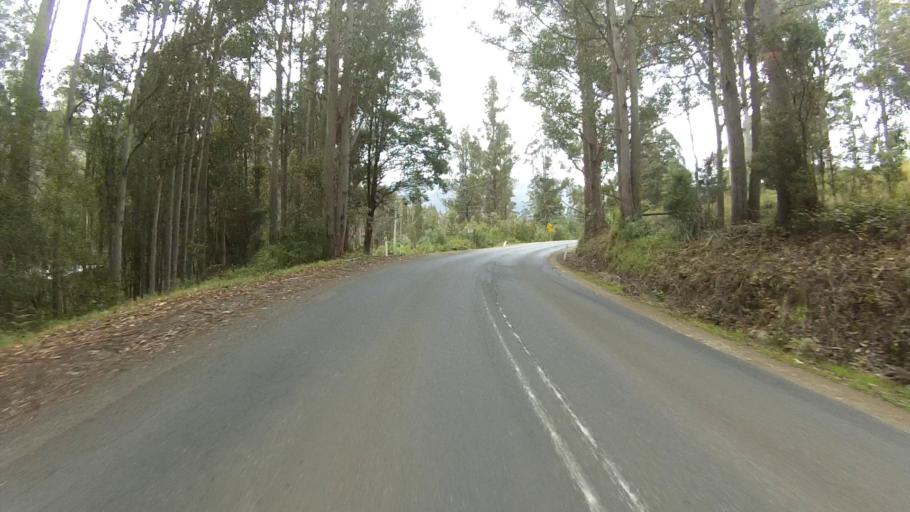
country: AU
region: Tasmania
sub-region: Huon Valley
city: Cygnet
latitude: -43.1383
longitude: 147.1518
